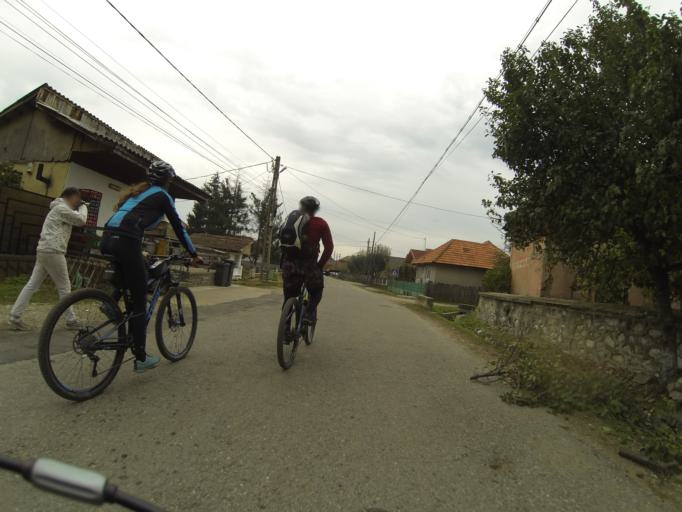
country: RO
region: Gorj
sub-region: Comuna Tismana
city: Pocruia
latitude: 45.0453
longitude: 22.9228
